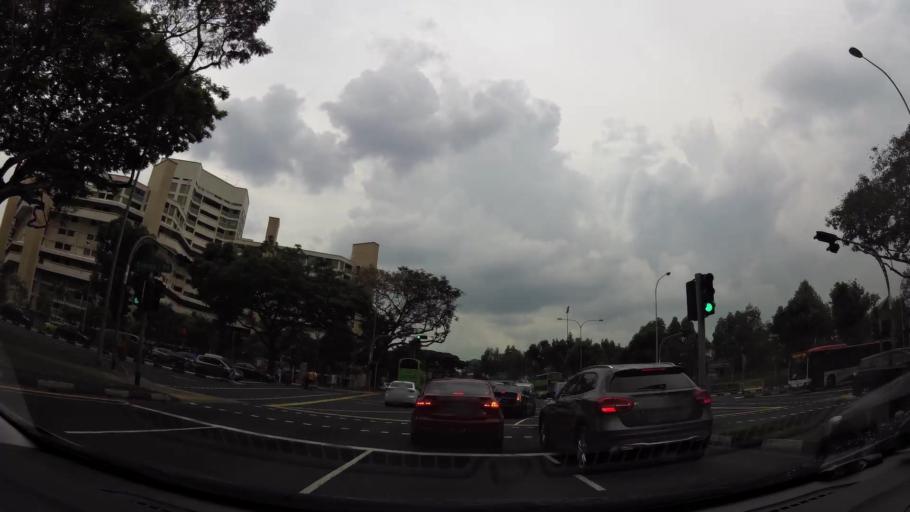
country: SG
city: Singapore
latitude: 1.3554
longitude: 103.8733
